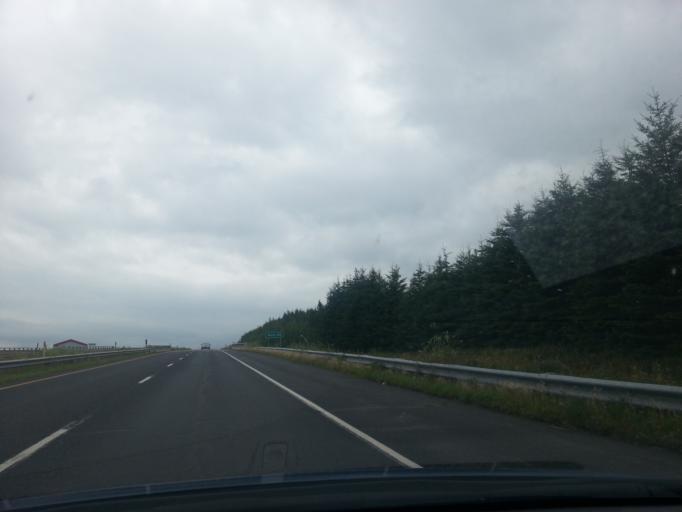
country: US
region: Maine
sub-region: Aroostook County
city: Limestone
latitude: 47.0425
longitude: -67.7674
